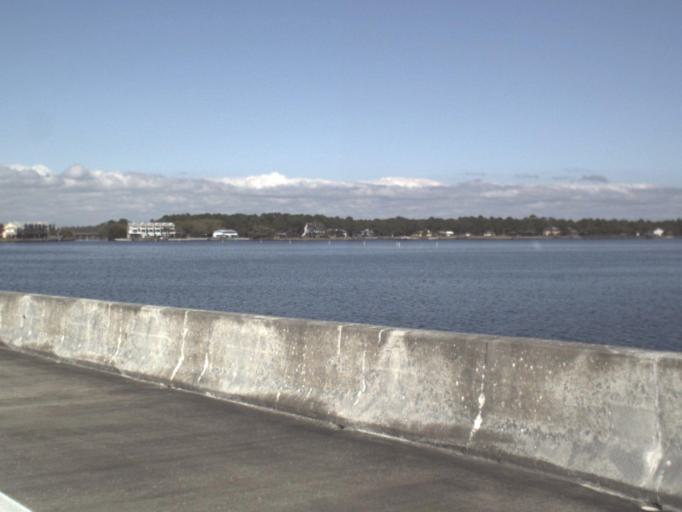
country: US
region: Florida
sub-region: Wakulla County
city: Crawfordville
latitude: 29.9715
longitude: -84.3837
